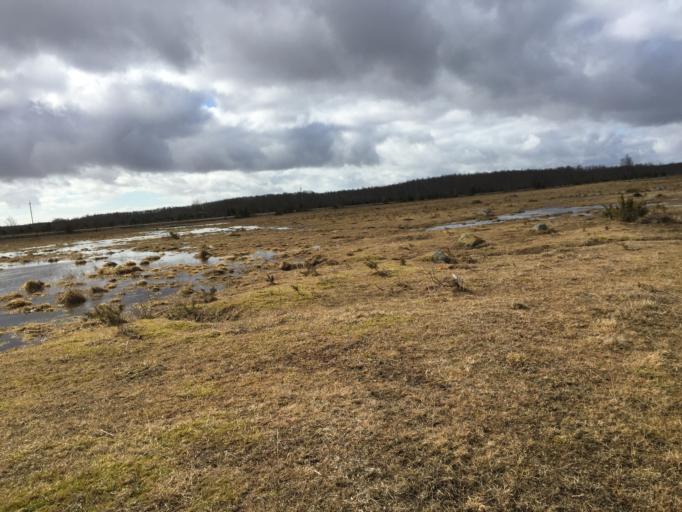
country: EE
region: Laeaene
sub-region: Ridala Parish
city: Uuemoisa
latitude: 58.7271
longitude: 23.5999
